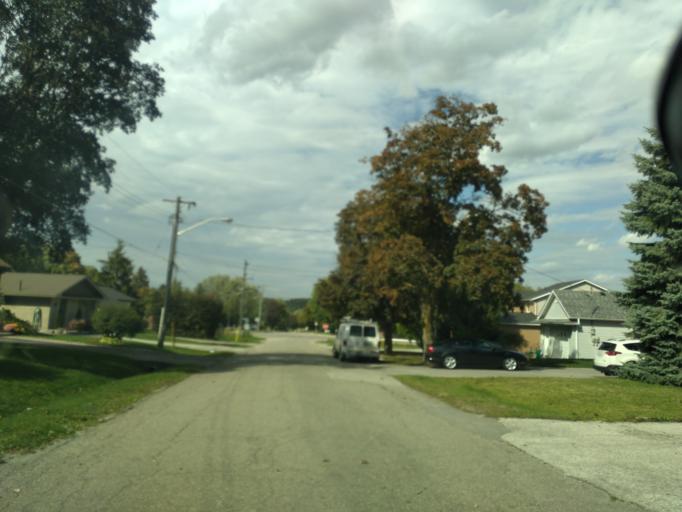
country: CA
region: Ontario
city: Newmarket
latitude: 44.0960
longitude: -79.4815
